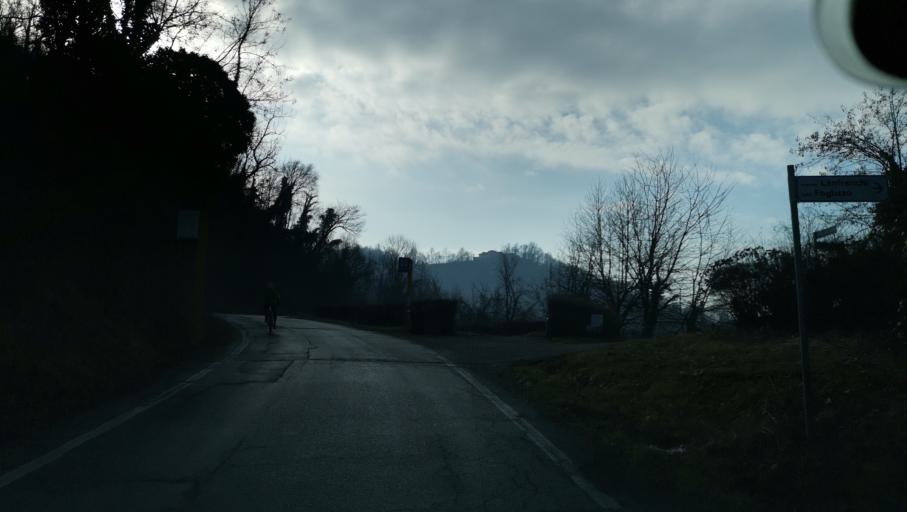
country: IT
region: Piedmont
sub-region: Provincia di Torino
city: Sciolze
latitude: 45.0997
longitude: 7.8903
